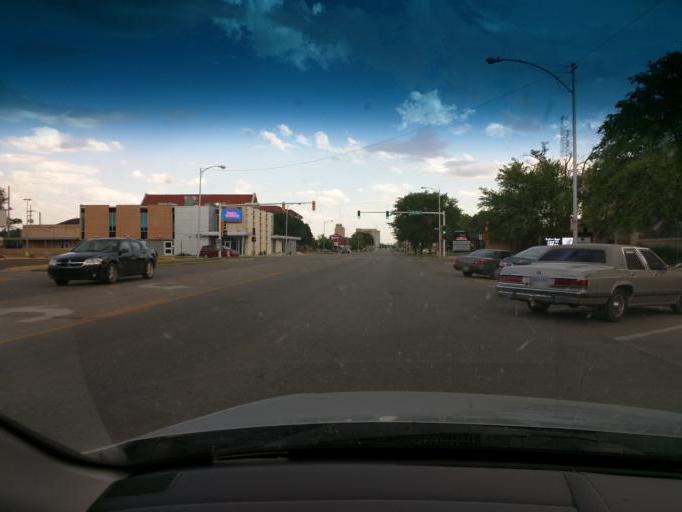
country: US
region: Kansas
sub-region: Reno County
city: Hutchinson
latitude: 38.0635
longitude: -97.9319
